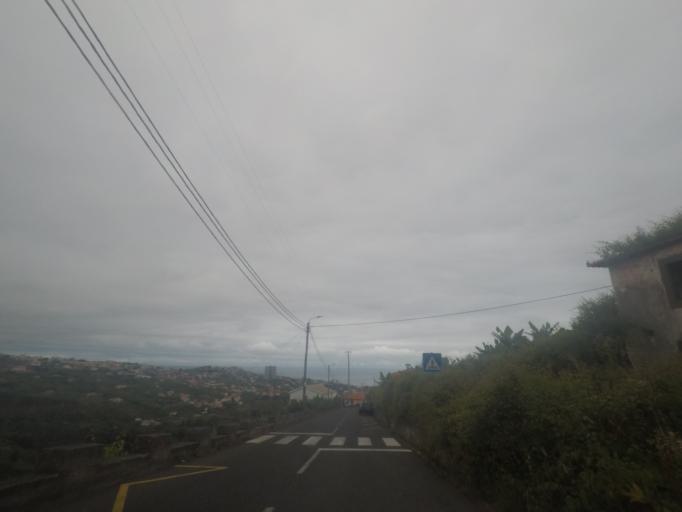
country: PT
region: Madeira
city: Camara de Lobos
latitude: 32.6651
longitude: -16.9641
